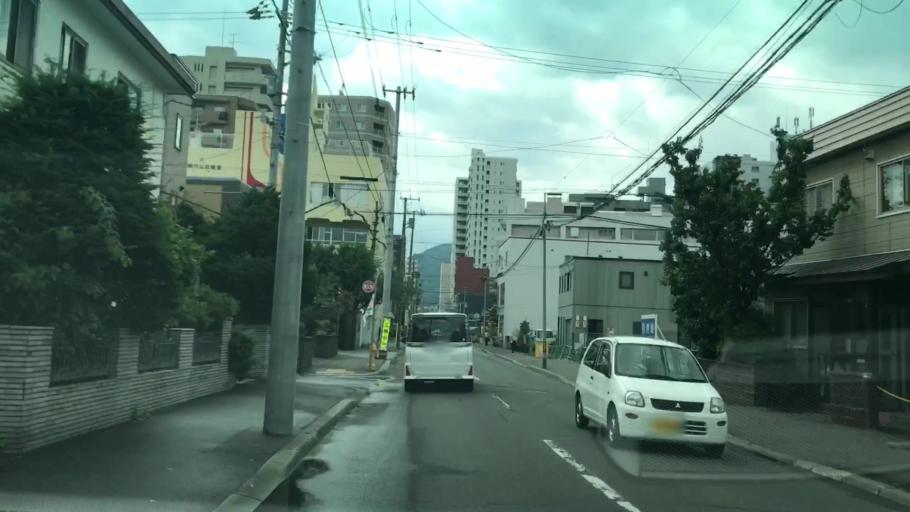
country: JP
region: Hokkaido
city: Sapporo
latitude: 43.0599
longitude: 141.3209
